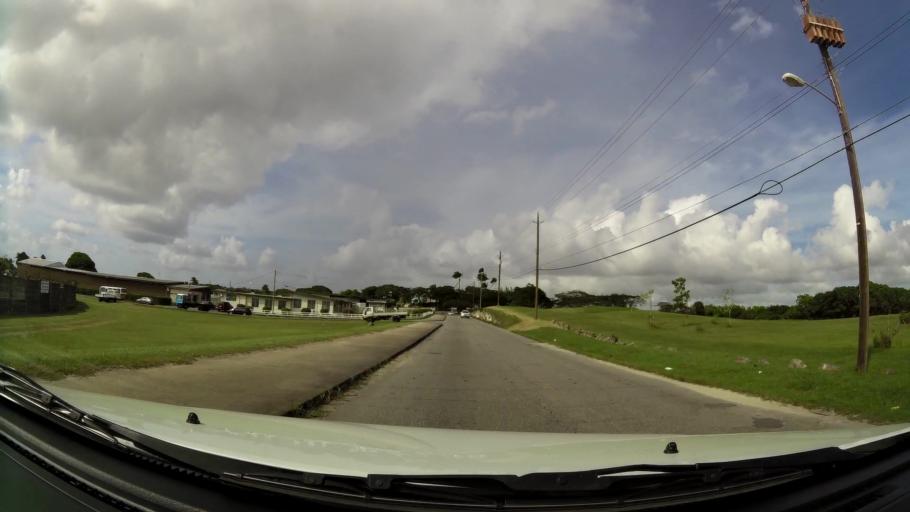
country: BB
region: Saint Michael
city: Bridgetown
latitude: 13.1213
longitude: -59.6039
